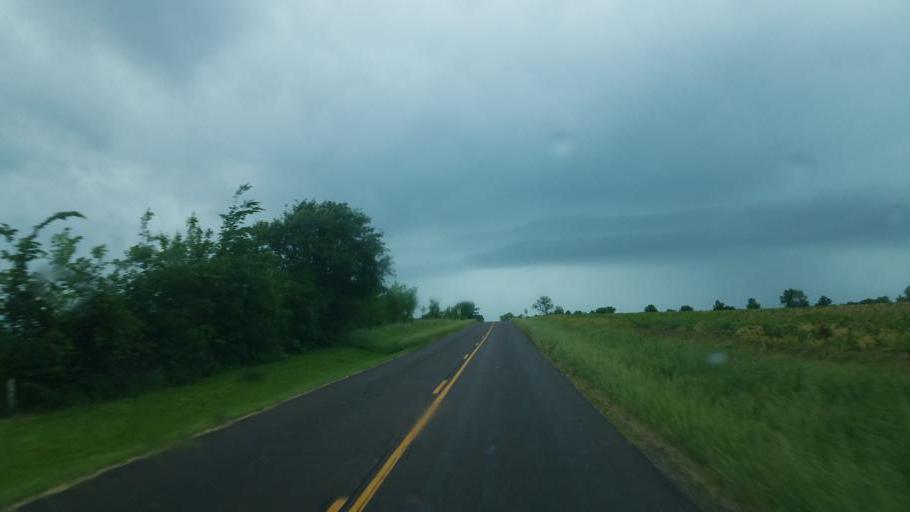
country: US
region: Missouri
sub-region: Moniteau County
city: California
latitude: 38.8115
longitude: -92.6007
